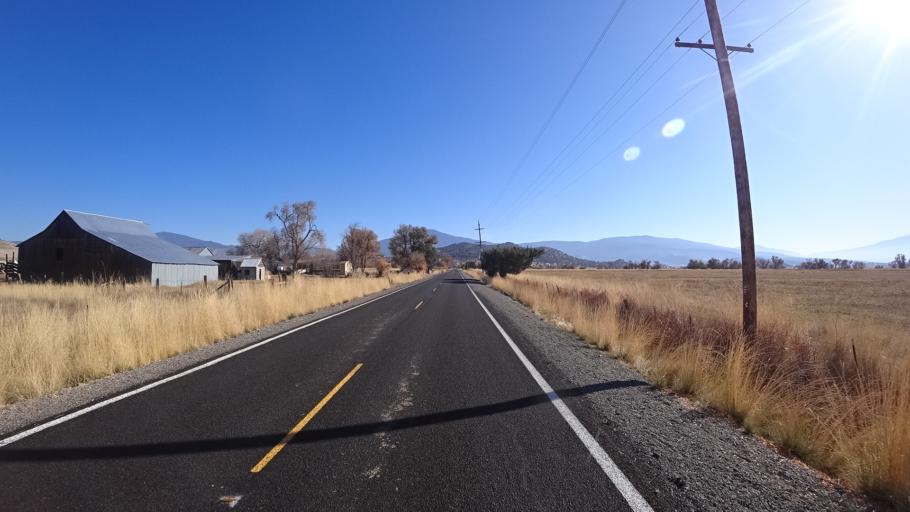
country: US
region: California
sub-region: Siskiyou County
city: Montague
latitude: 41.7115
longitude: -122.3962
